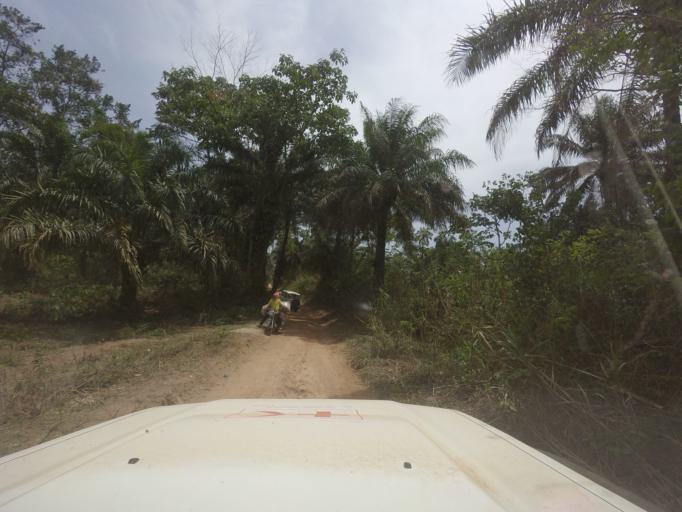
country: SL
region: Eastern Province
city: Buedu
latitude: 8.4824
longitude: -10.3355
